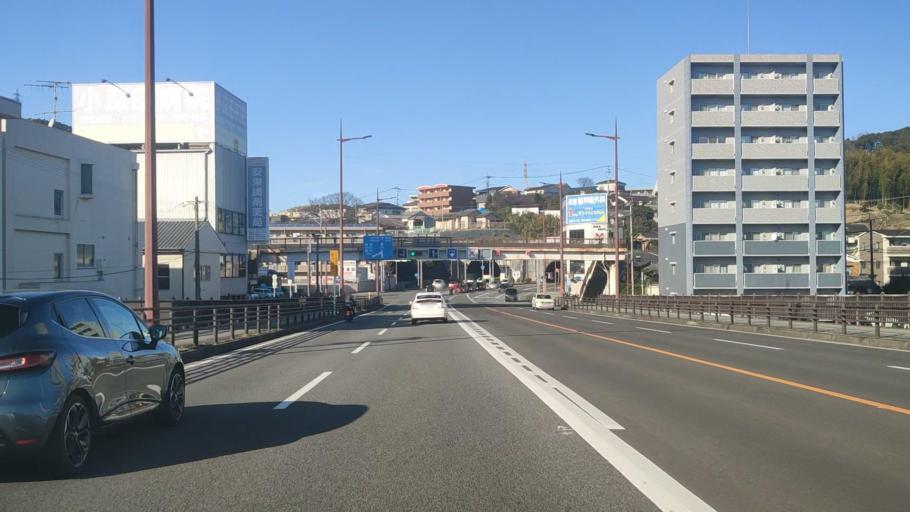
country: JP
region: Oita
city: Oita
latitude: 33.2177
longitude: 131.5952
